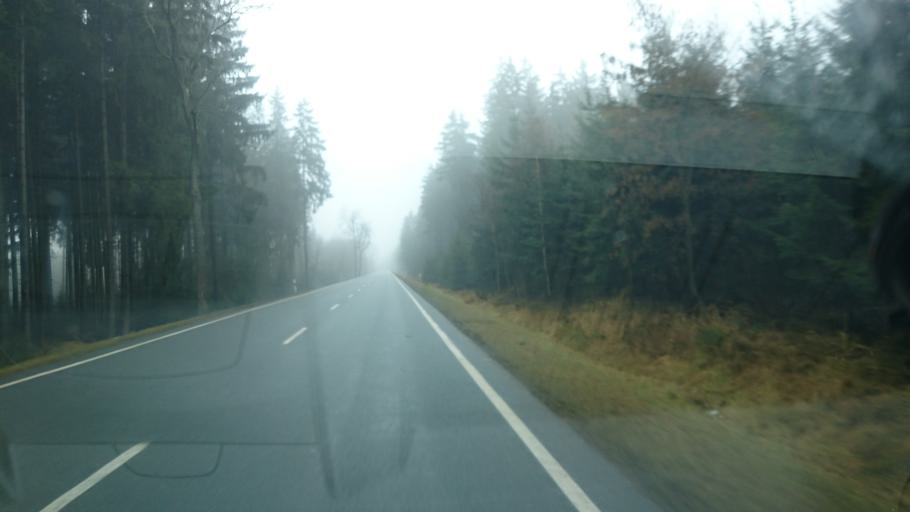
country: DE
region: Thuringia
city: Tanna
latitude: 50.4753
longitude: 11.8387
